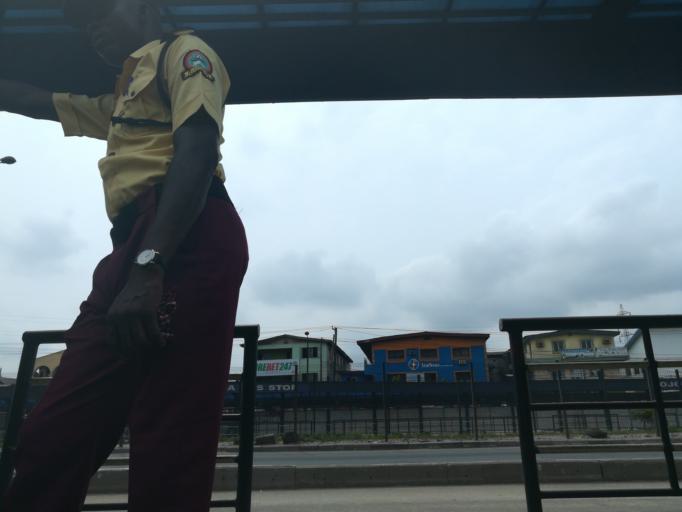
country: NG
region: Lagos
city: Ojota
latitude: 6.5878
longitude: 3.3787
